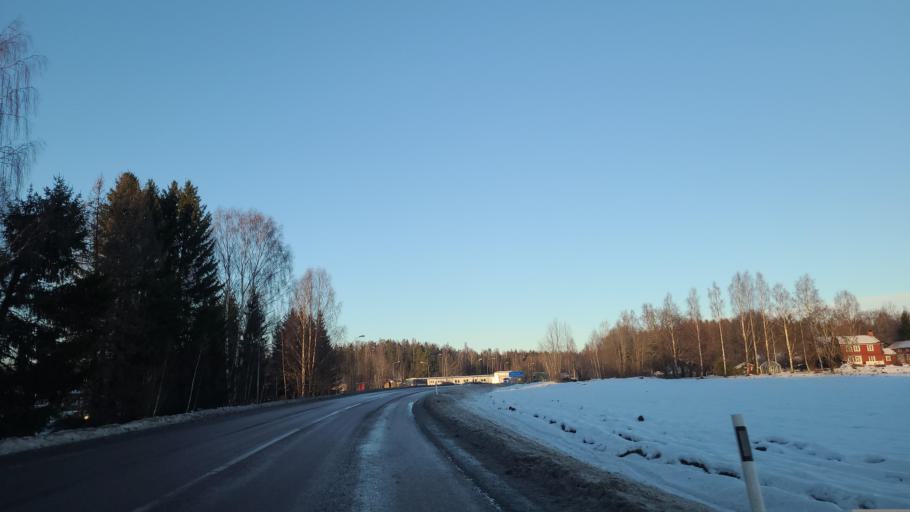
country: SE
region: Gaevleborg
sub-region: Soderhamns Kommun
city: Soderhamn
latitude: 61.2813
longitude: 16.9702
